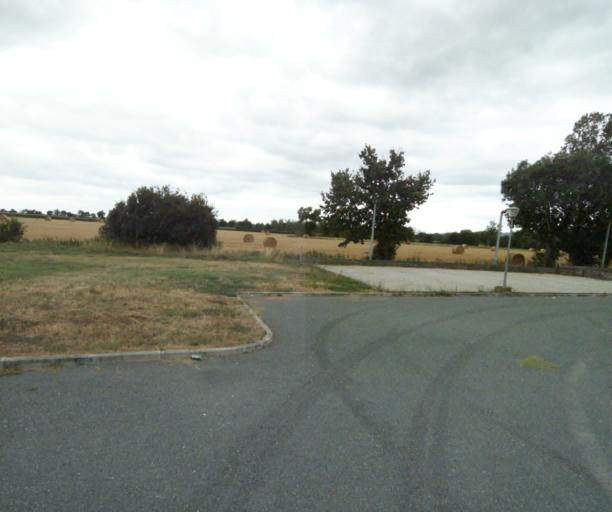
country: FR
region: Midi-Pyrenees
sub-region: Departement du Tarn
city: Soreze
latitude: 43.4583
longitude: 2.0468
